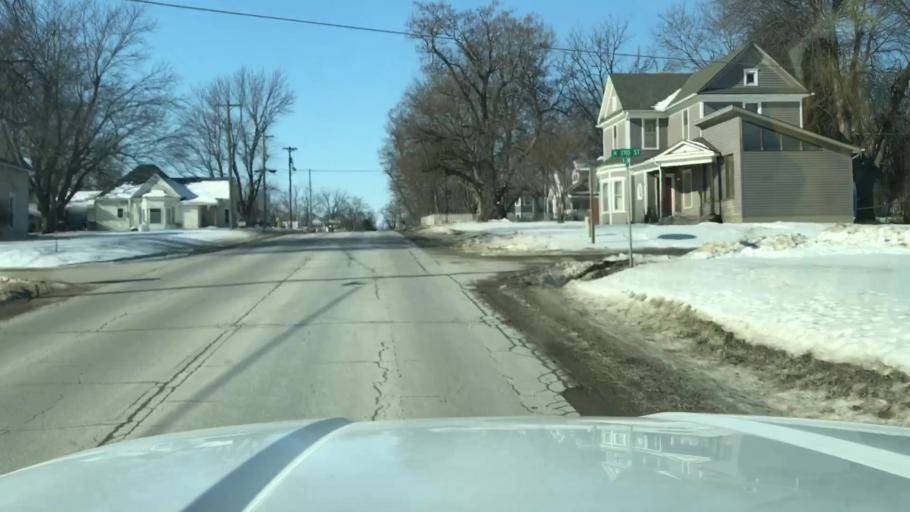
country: US
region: Missouri
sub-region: Andrew County
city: Savannah
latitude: 39.9467
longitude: -94.8271
